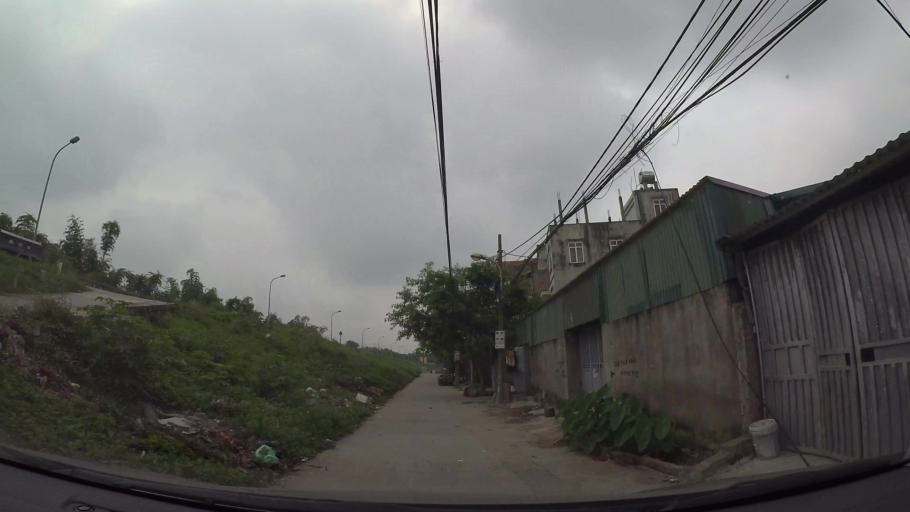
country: VN
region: Ha Noi
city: Trau Quy
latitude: 21.0532
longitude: 105.9227
